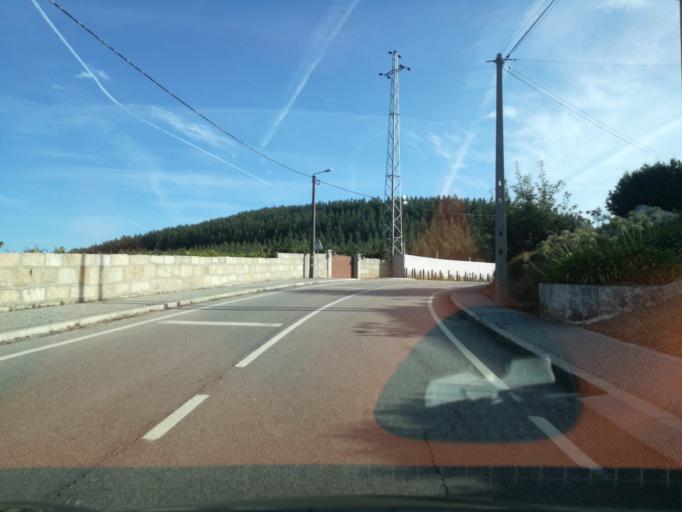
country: PT
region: Porto
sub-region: Trofa
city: Sao Romao do Coronado
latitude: 41.2789
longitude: -8.5247
